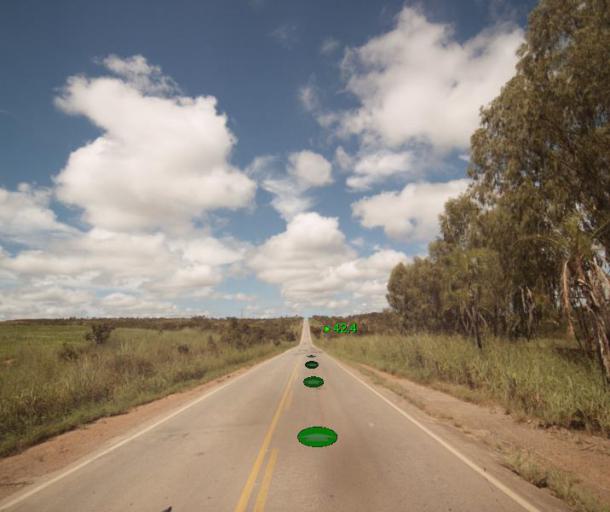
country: BR
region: Goias
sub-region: Padre Bernardo
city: Padre Bernardo
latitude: -15.1996
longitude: -48.2836
